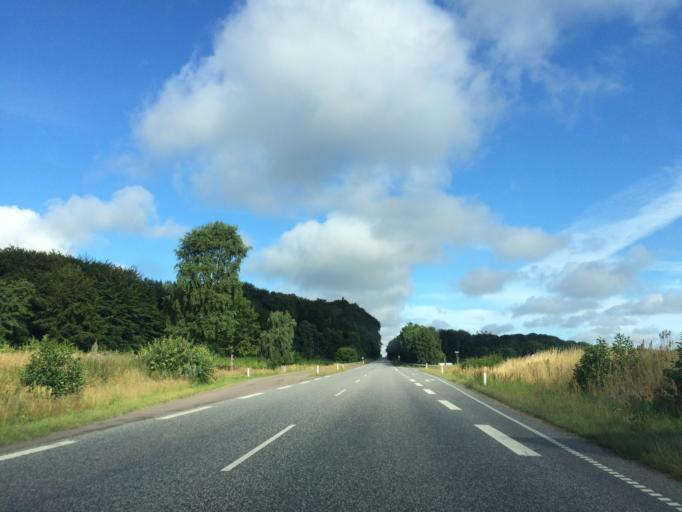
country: DK
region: Central Jutland
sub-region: Viborg Kommune
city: Bjerringbro
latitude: 56.3178
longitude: 9.5752
